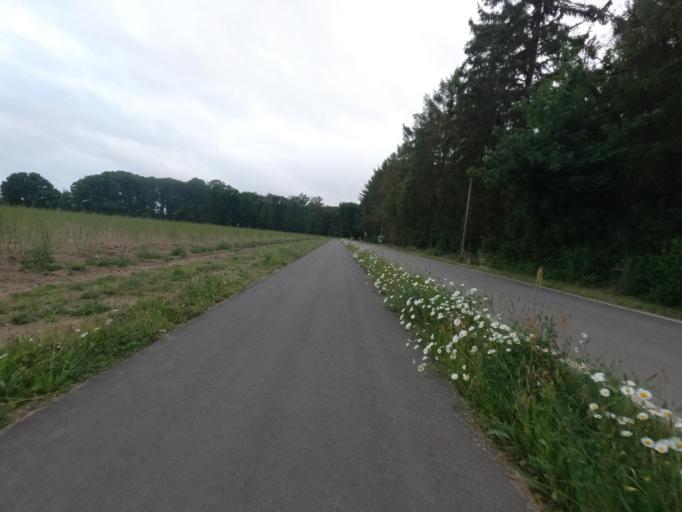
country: NL
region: Limburg
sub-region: Gemeente Roerdalen
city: Vlodrop
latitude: 51.1317
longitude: 6.1056
